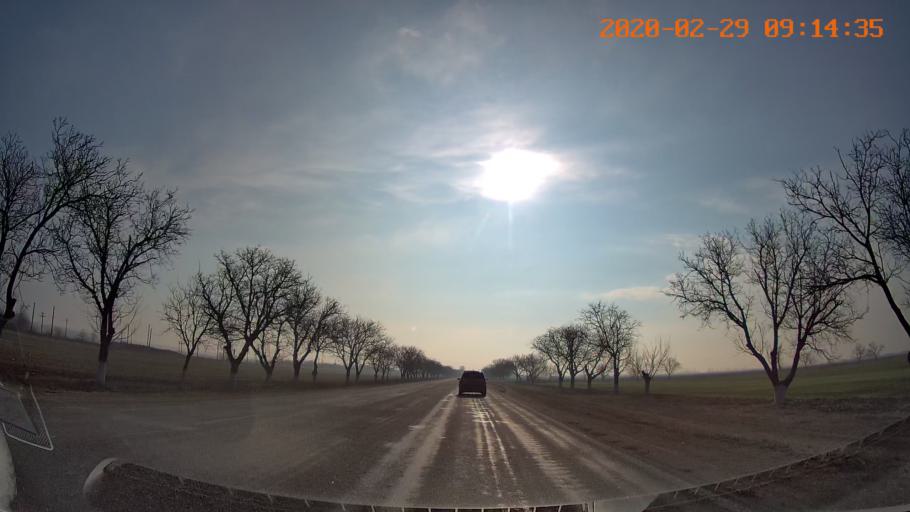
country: MD
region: Telenesti
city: Pervomaisc
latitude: 46.8076
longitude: 29.8550
